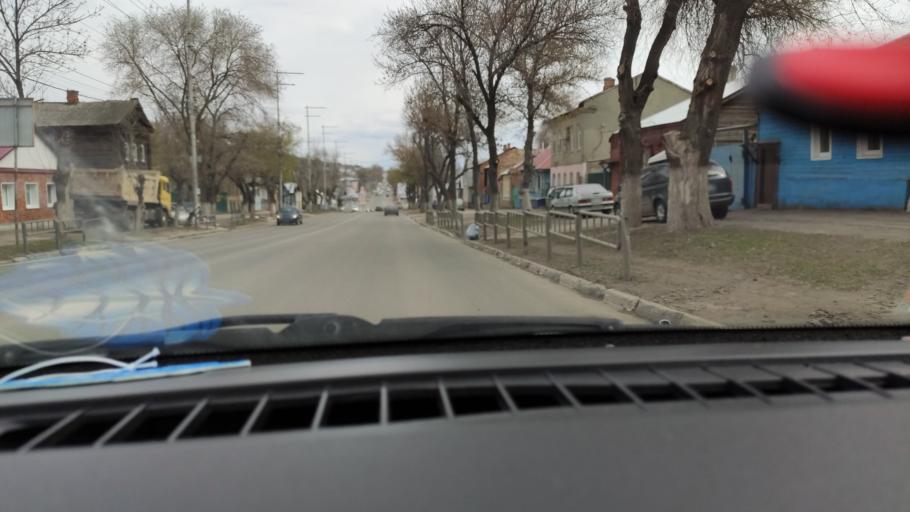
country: RU
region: Saratov
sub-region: Saratovskiy Rayon
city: Saratov
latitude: 51.5443
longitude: 46.0324
